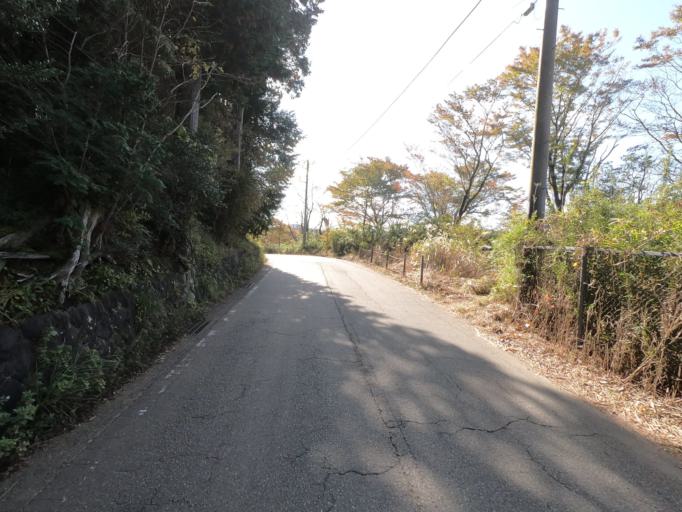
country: JP
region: Kanagawa
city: Hakone
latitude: 35.2071
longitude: 139.0170
